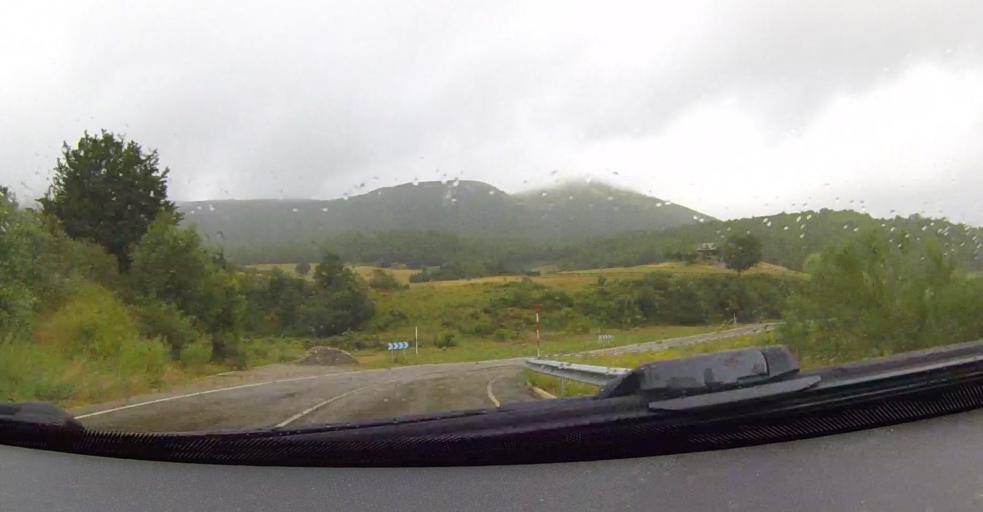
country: ES
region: Castille and Leon
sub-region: Provincia de Leon
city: Marana
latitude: 43.0720
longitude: -5.1969
